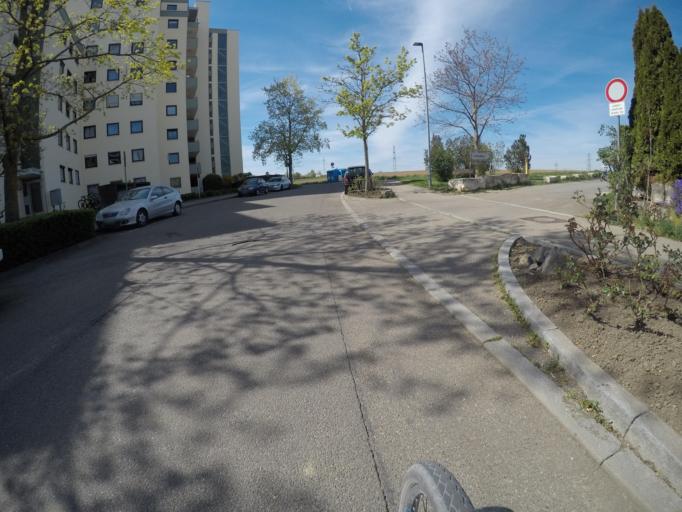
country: DE
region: Baden-Wuerttemberg
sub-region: Regierungsbezirk Stuttgart
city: Ditzingen
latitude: 48.8392
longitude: 9.0414
